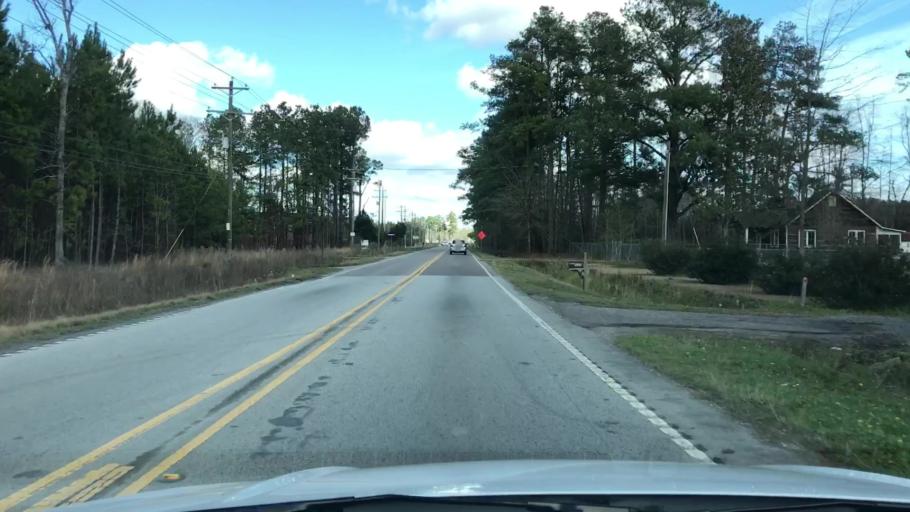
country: US
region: South Carolina
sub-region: Dorchester County
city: Summerville
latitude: 33.0857
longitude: -80.2026
